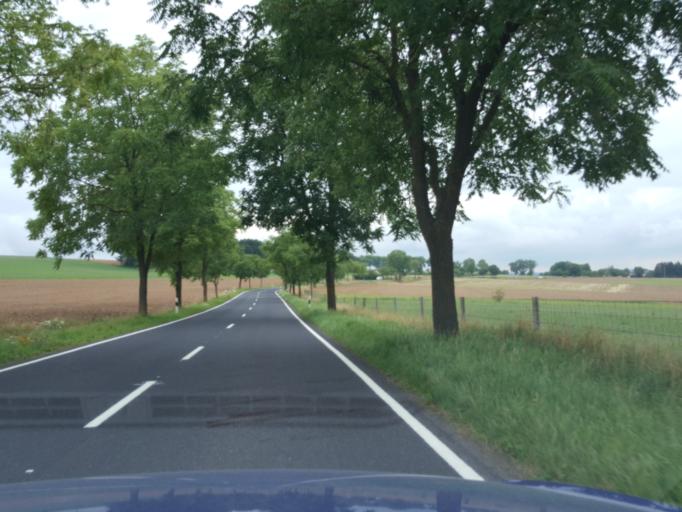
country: LU
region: Luxembourg
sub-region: Canton de Capellen
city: Kehlen
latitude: 49.6820
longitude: 6.0549
